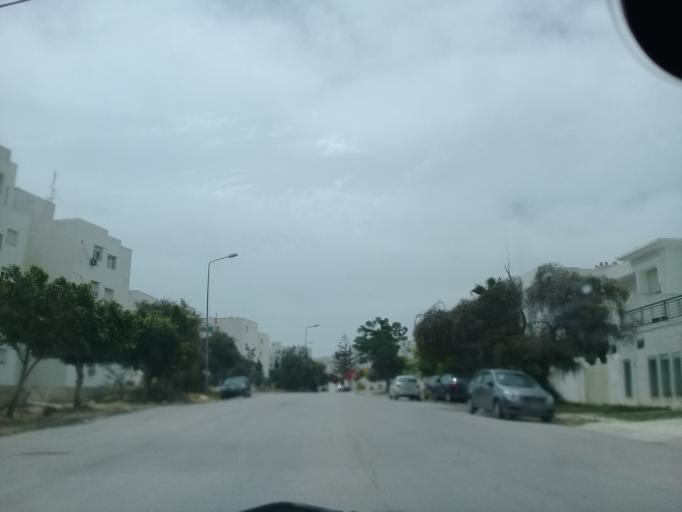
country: TN
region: Tunis
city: Tunis
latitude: 36.8385
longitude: 10.1524
